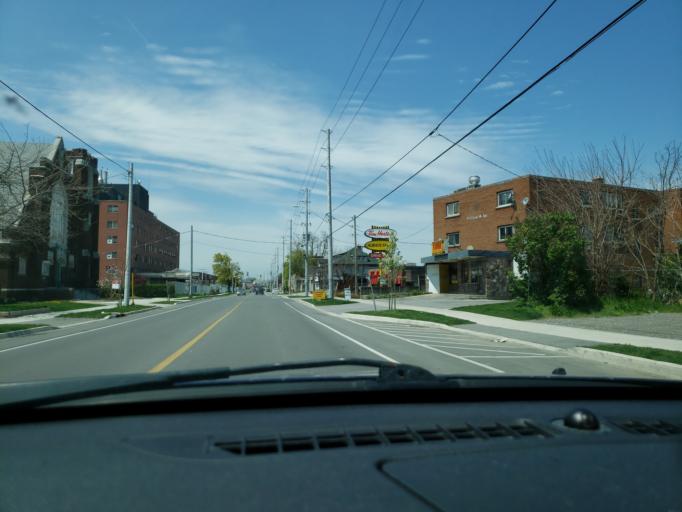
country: CA
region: Ontario
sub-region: Regional Municipality of Niagara
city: St. Catharines
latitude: 43.1621
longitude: -79.2266
